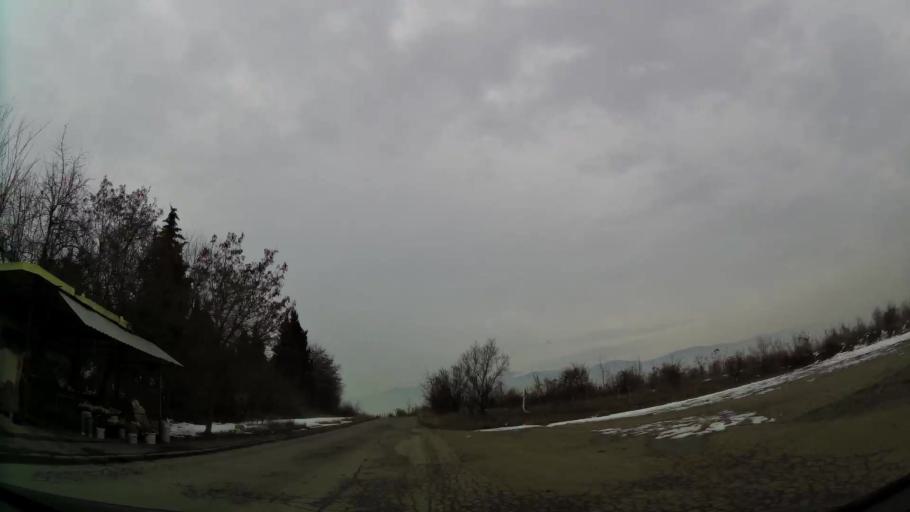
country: MK
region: Butel
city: Butel
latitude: 42.0382
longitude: 21.4372
